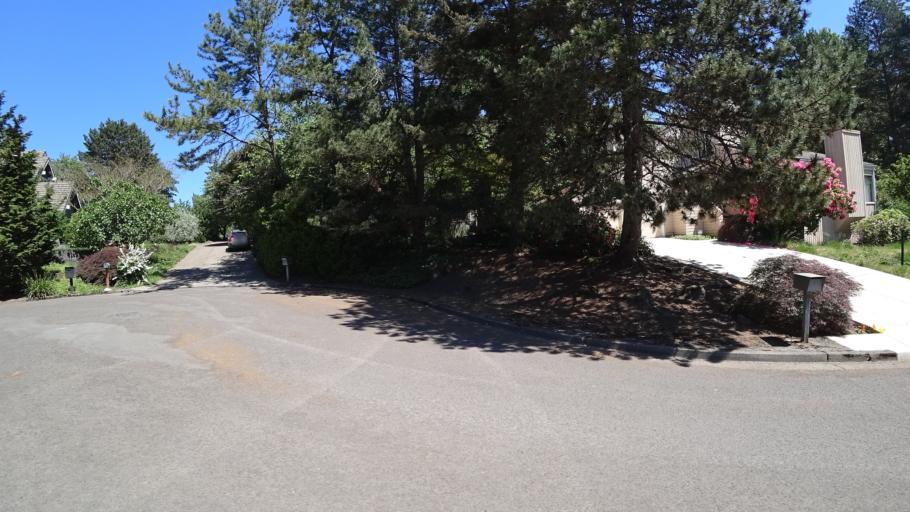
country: US
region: Oregon
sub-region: Washington County
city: Raleigh Hills
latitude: 45.4879
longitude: -122.7122
